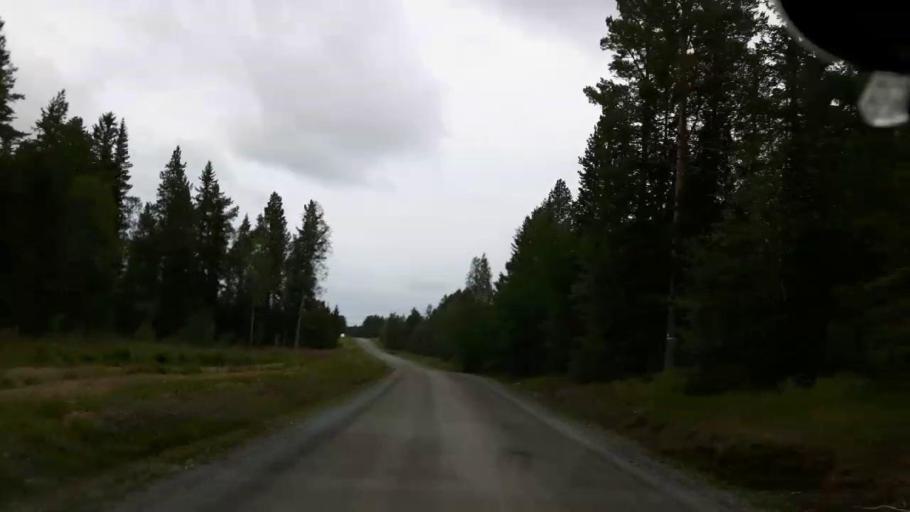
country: SE
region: Jaemtland
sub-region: OEstersunds Kommun
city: Ostersund
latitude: 63.1046
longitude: 14.5465
